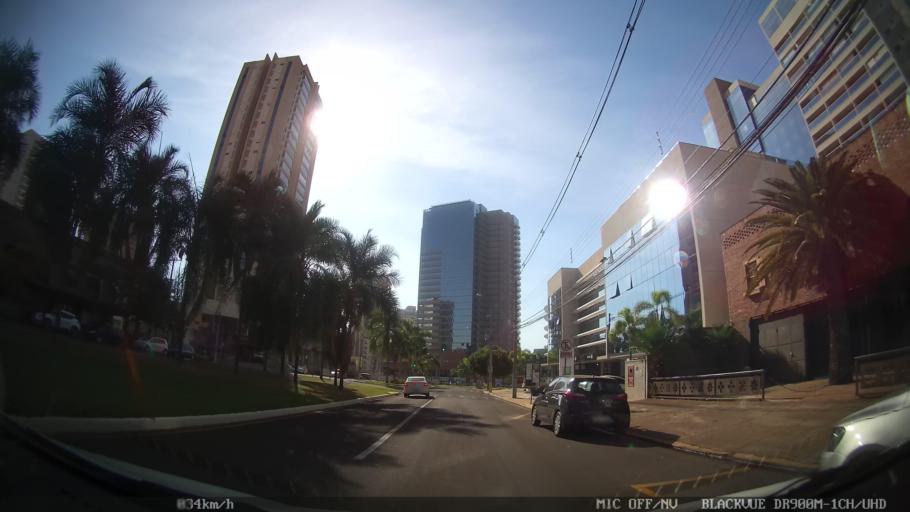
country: BR
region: Sao Paulo
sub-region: Ribeirao Preto
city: Ribeirao Preto
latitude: -21.2103
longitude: -47.8002
